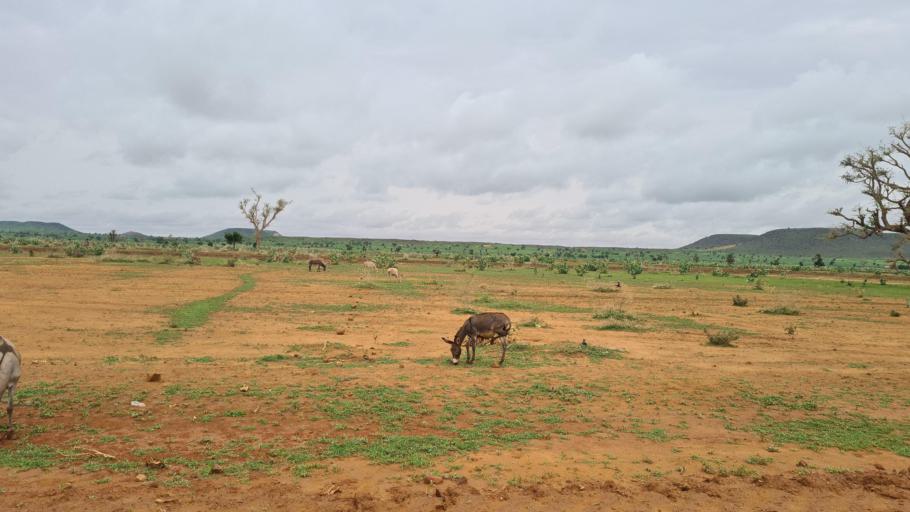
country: NE
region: Tahoua
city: Birni N Konni
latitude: 13.8121
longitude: 5.2431
